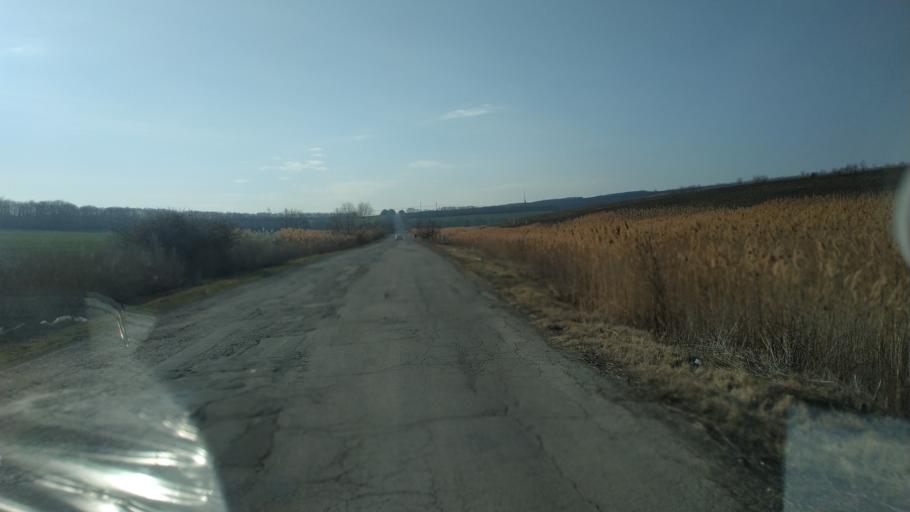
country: MD
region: Chisinau
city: Singera
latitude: 46.8841
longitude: 29.0392
